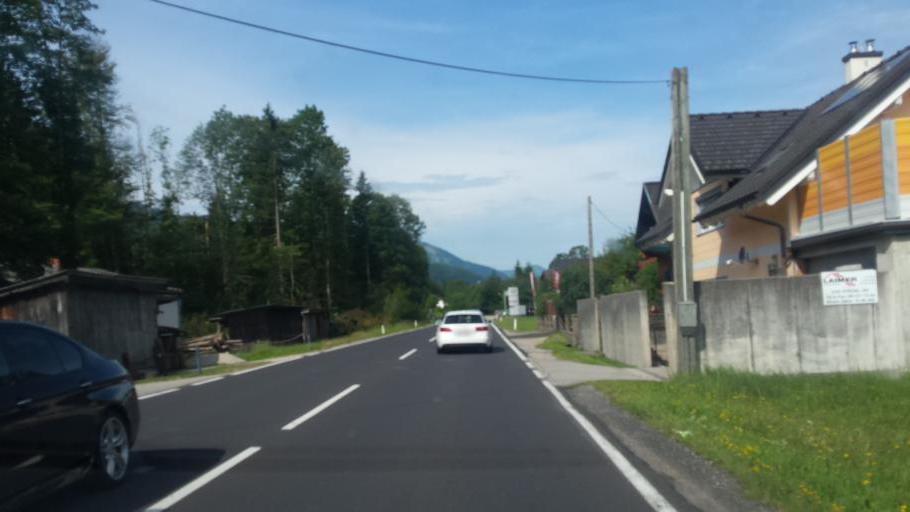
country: AT
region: Upper Austria
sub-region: Politischer Bezirk Gmunden
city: Bad Ischl
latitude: 47.7174
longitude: 13.5791
